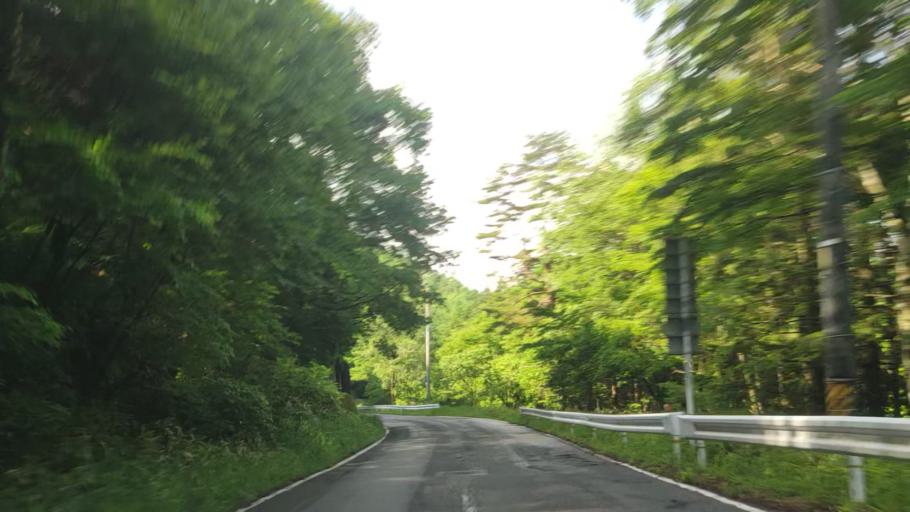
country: JP
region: Nagano
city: Suwa
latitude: 36.0828
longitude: 138.1414
